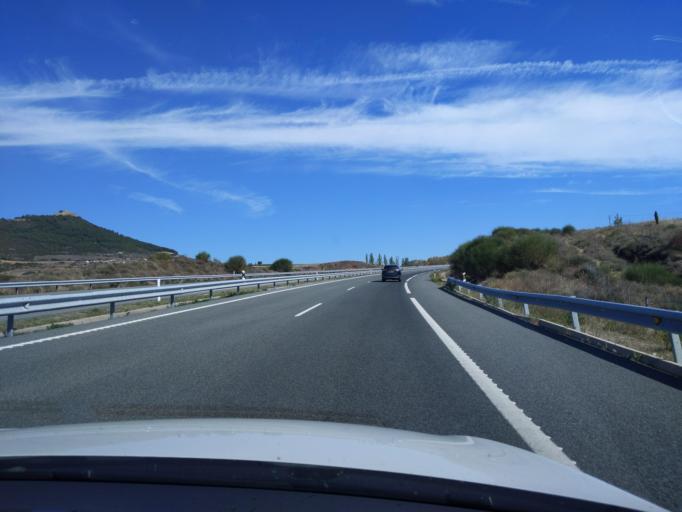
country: ES
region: Navarre
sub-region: Provincia de Navarra
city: Villamayor de Monjardin
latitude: 42.6158
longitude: -2.1098
